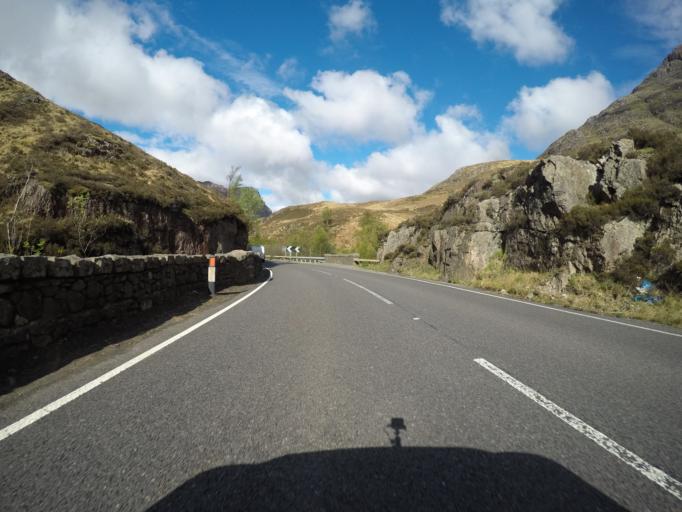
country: GB
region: Scotland
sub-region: Highland
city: Fort William
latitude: 56.6642
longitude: -4.9618
